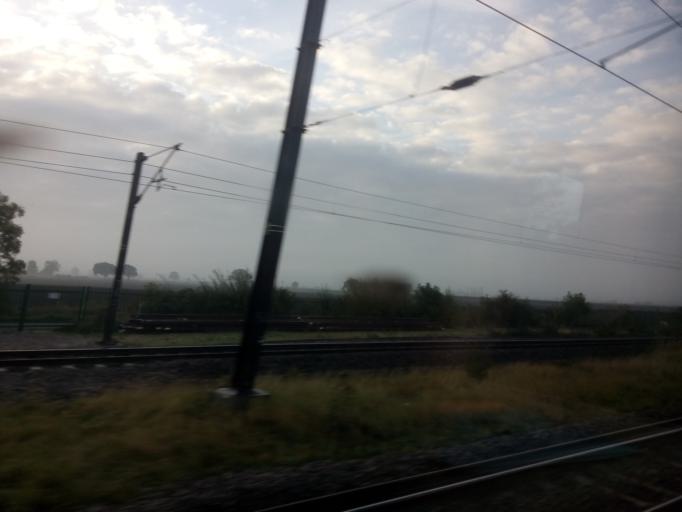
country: GB
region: England
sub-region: City of York
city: Copmanthorpe
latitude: 53.9113
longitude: -1.1389
